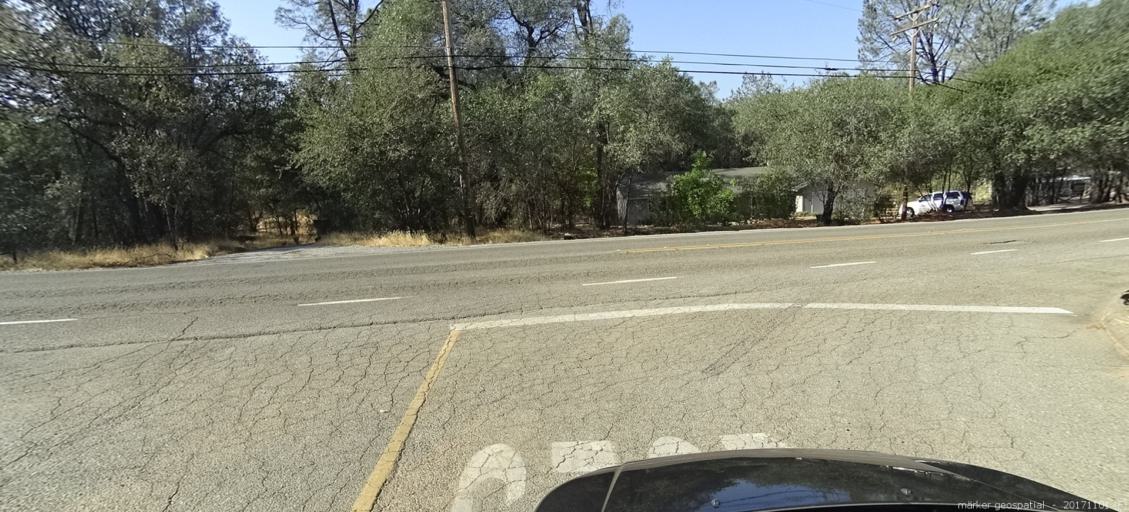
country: US
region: California
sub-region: Shasta County
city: Shasta Lake
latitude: 40.6870
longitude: -122.3163
